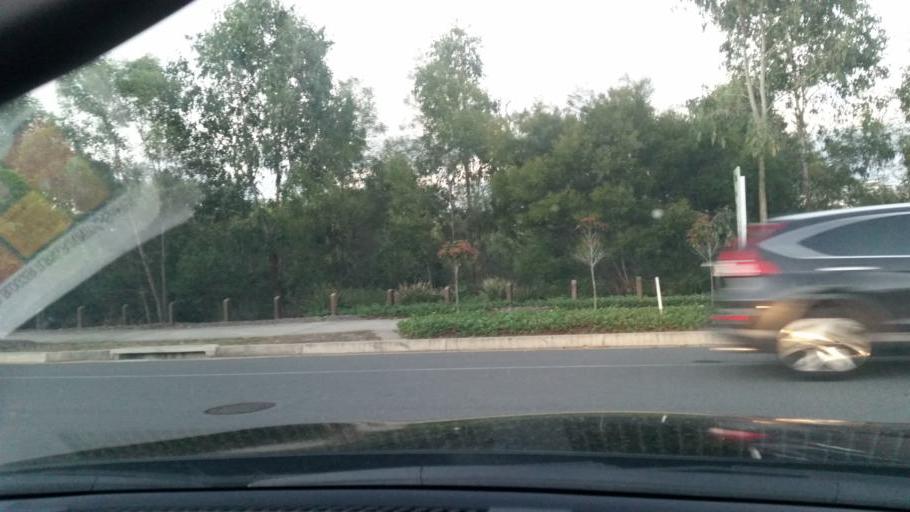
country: AU
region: Queensland
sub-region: Brisbane
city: Mackenzie
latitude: -27.5671
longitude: 153.1132
